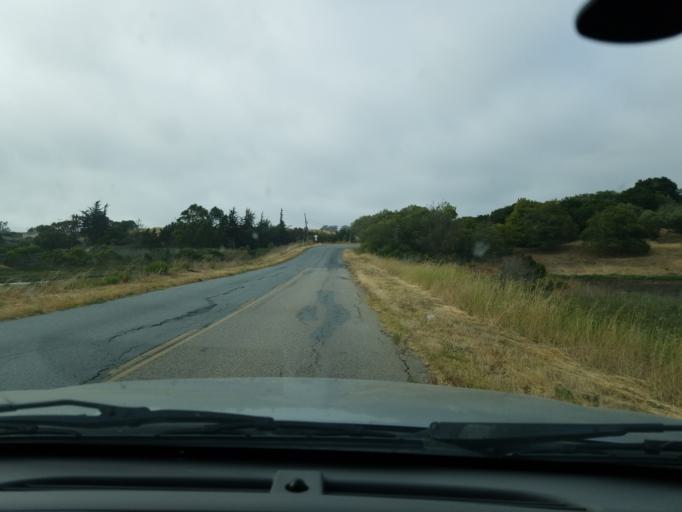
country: US
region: California
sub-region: Monterey County
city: Las Lomas
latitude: 36.8577
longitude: -121.7549
